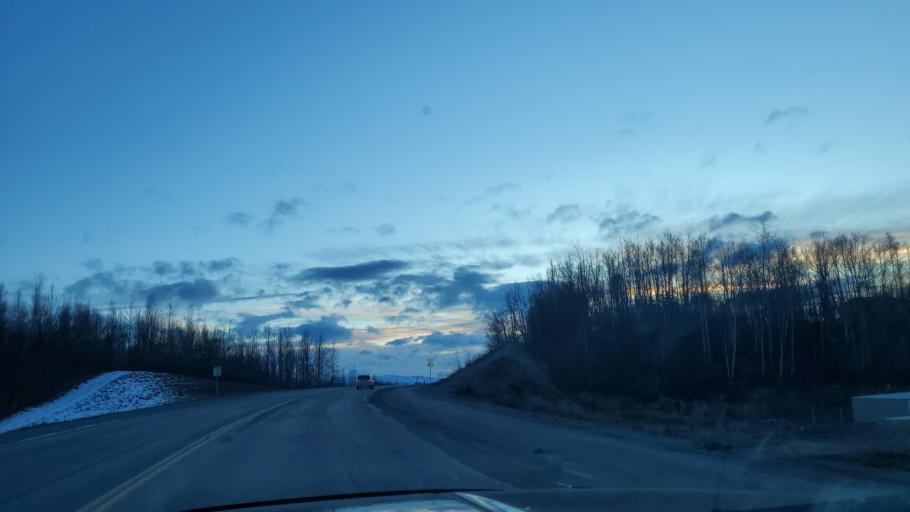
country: US
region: Alaska
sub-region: Matanuska-Susitna Borough
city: Wasilla
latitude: 61.5756
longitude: -149.4415
